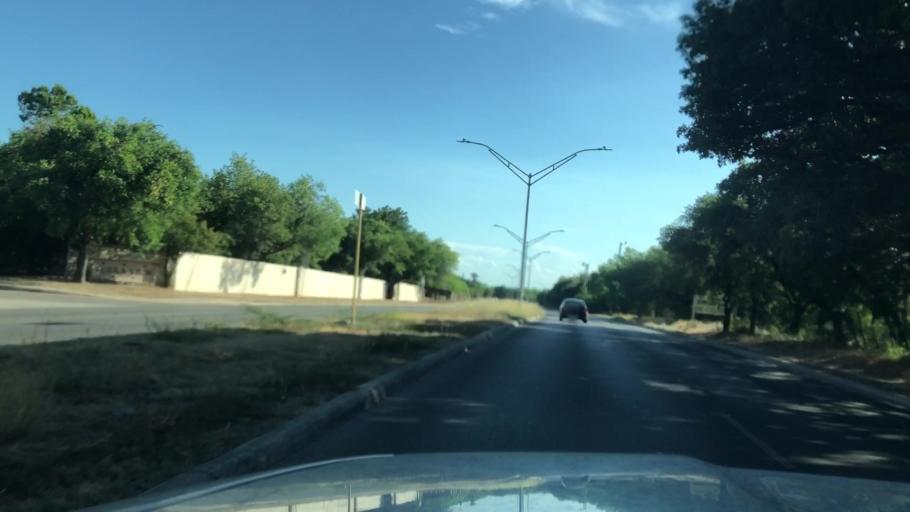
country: US
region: Texas
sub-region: Bexar County
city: Leon Valley
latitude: 29.5444
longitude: -98.6263
